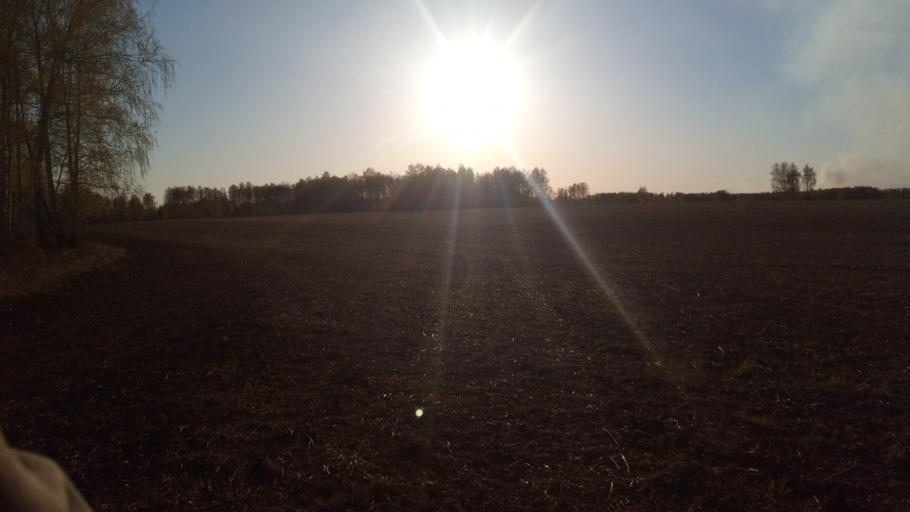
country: RU
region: Chelyabinsk
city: Timiryazevskiy
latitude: 54.9949
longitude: 60.8676
